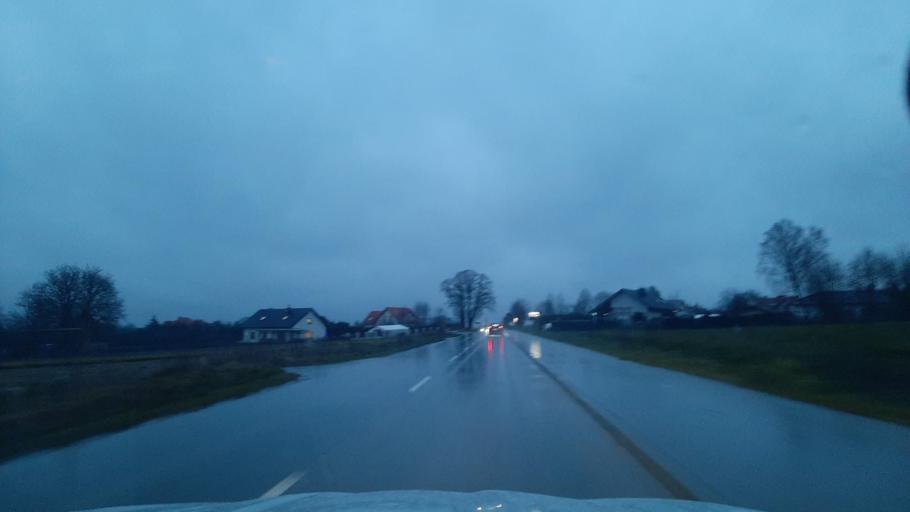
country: PL
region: Lublin Voivodeship
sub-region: Powiat lubelski
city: Jastkow
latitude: 51.3290
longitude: 22.5164
